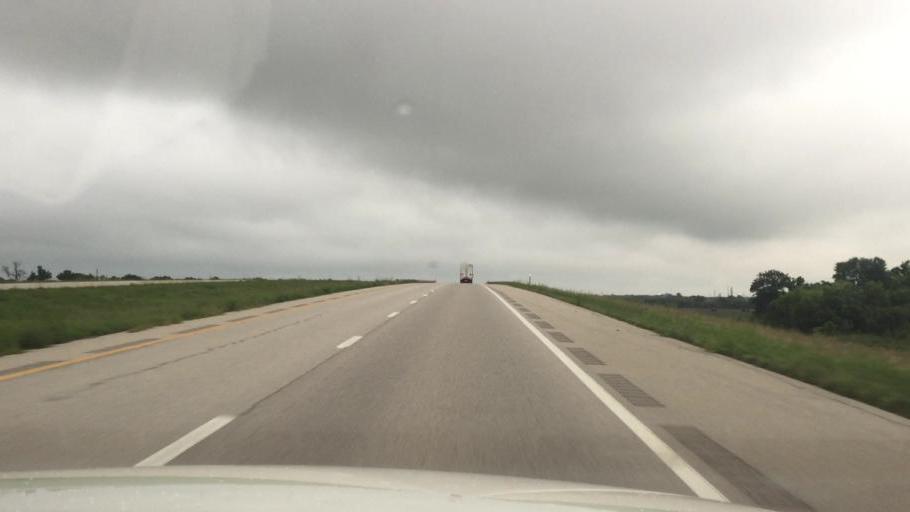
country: US
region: Kansas
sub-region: Montgomery County
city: Coffeyville
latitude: 37.0889
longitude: -95.5899
